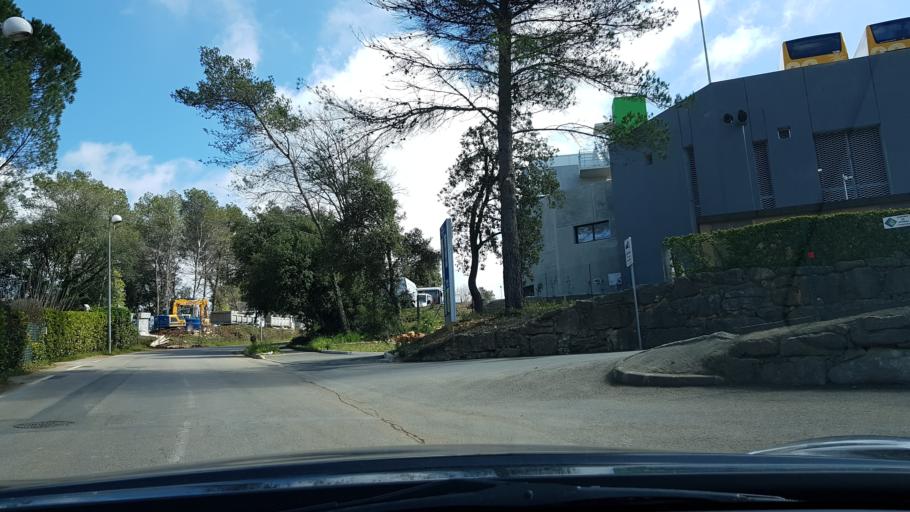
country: FR
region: Provence-Alpes-Cote d'Azur
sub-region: Departement des Alpes-Maritimes
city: Biot
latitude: 43.6084
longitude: 7.0740
